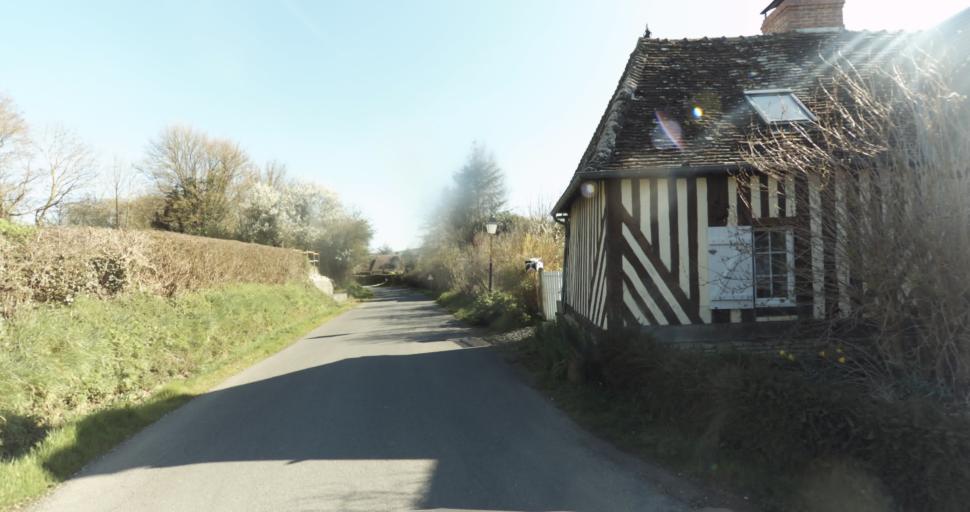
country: FR
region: Lower Normandy
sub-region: Departement du Calvados
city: Saint-Pierre-sur-Dives
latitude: 49.0401
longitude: 0.0398
